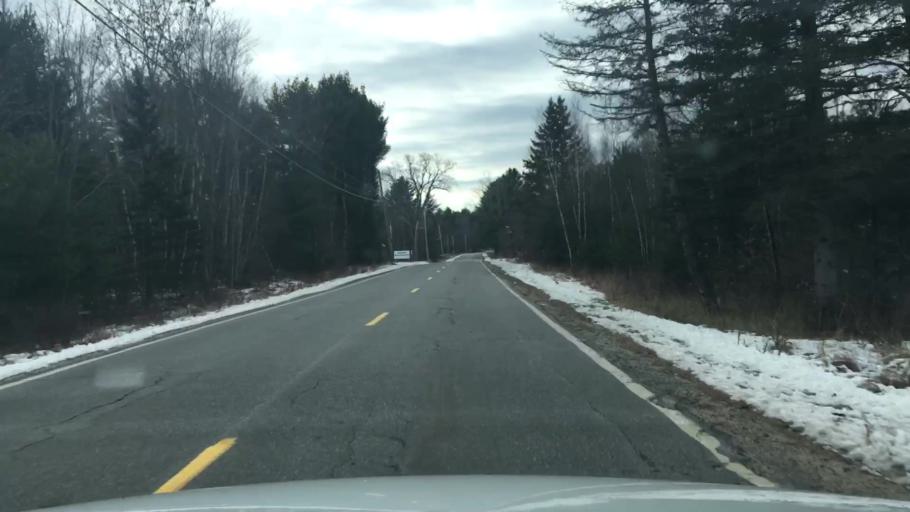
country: US
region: Maine
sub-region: Oxford County
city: Canton
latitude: 44.4523
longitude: -70.3038
